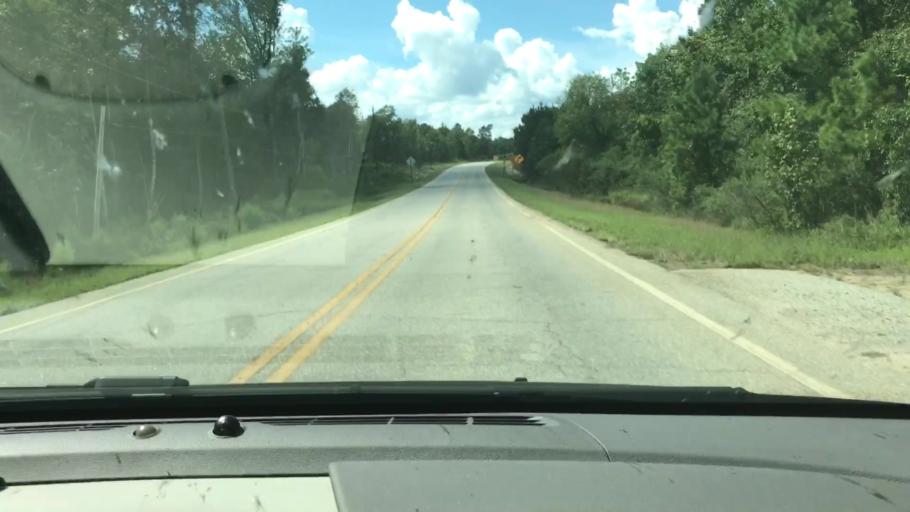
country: US
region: Georgia
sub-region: Quitman County
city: Georgetown
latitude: 31.7652
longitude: -85.0851
